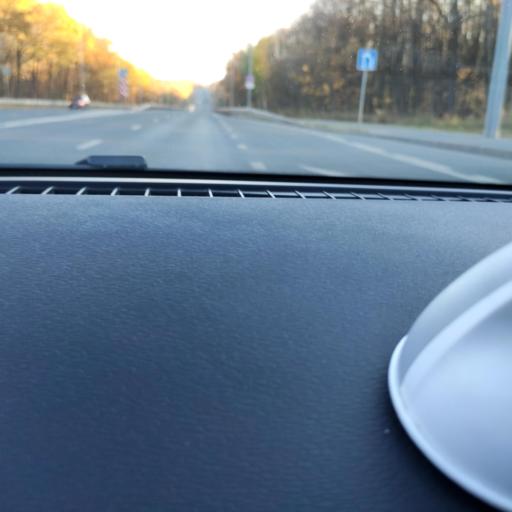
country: RU
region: Samara
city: Petra-Dubrava
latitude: 53.2946
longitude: 50.2458
